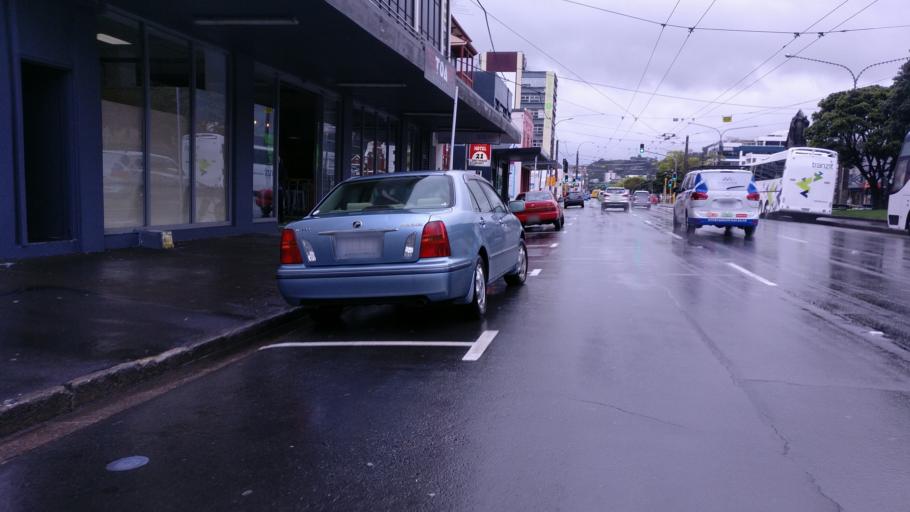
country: NZ
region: Wellington
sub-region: Wellington City
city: Wellington
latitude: -41.2947
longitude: 174.7837
